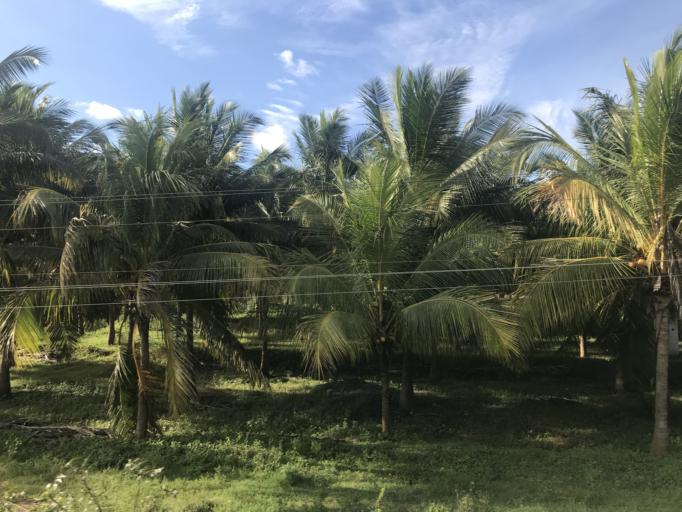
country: IN
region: Tamil Nadu
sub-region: Coimbatore
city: Madukkarai
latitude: 10.8830
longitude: 76.8695
